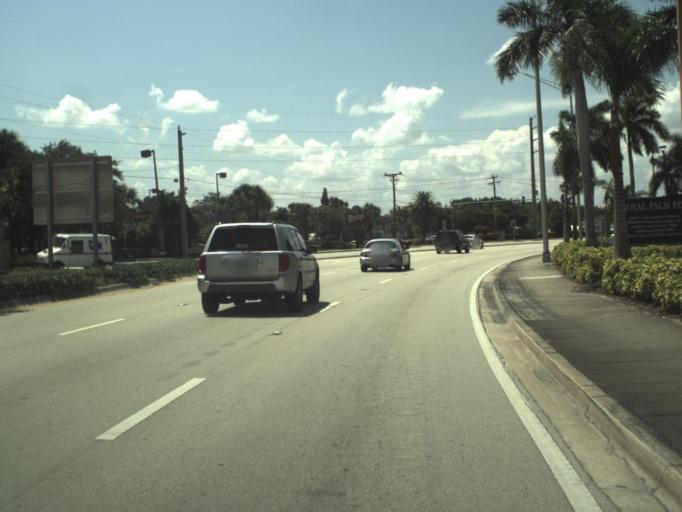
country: US
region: Florida
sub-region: Martin County
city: Stuart
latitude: 27.1924
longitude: -80.2555
